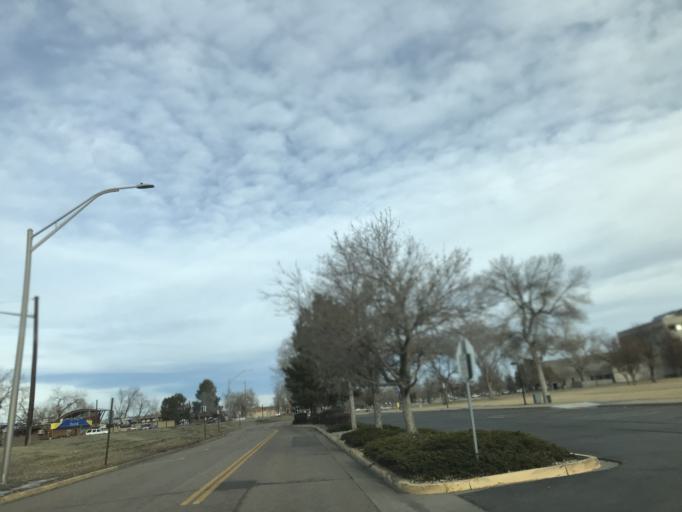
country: US
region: Colorado
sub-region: Arapahoe County
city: Littleton
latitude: 39.6066
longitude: -105.0203
